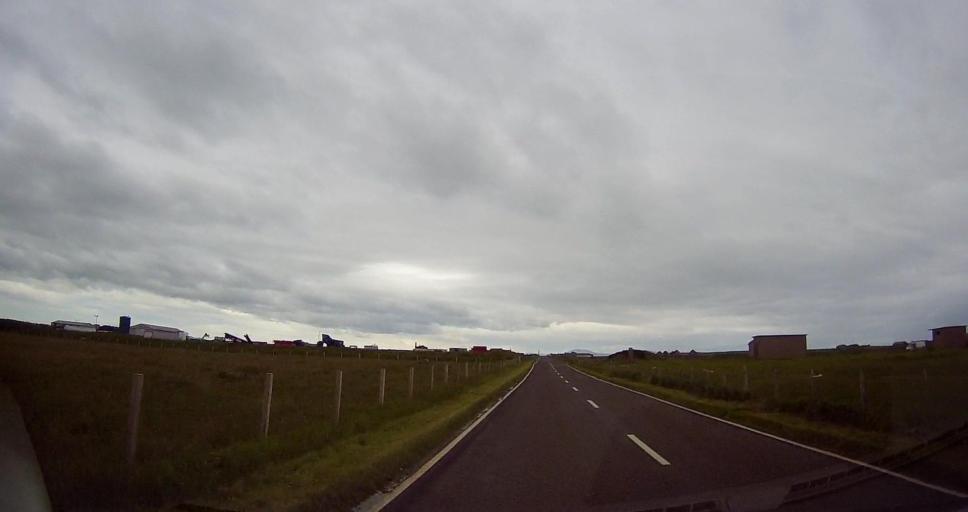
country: GB
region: Scotland
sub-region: Orkney Islands
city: Stromness
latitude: 59.0873
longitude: -3.2754
